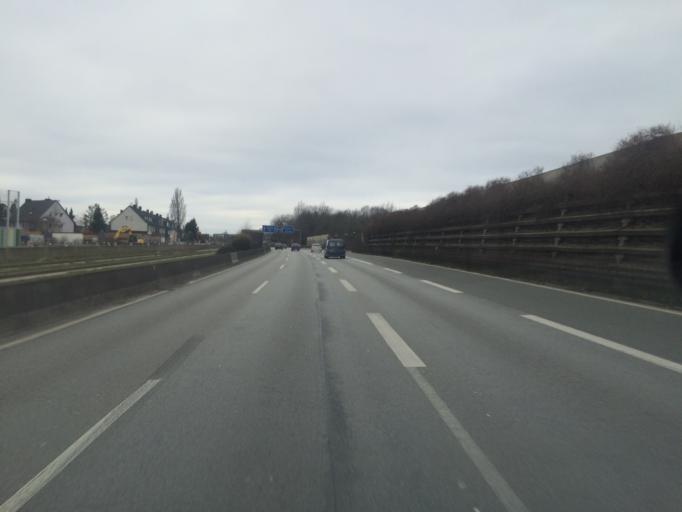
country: DE
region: North Rhine-Westphalia
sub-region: Regierungsbezirk Dusseldorf
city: Essen
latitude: 51.4601
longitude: 7.0536
